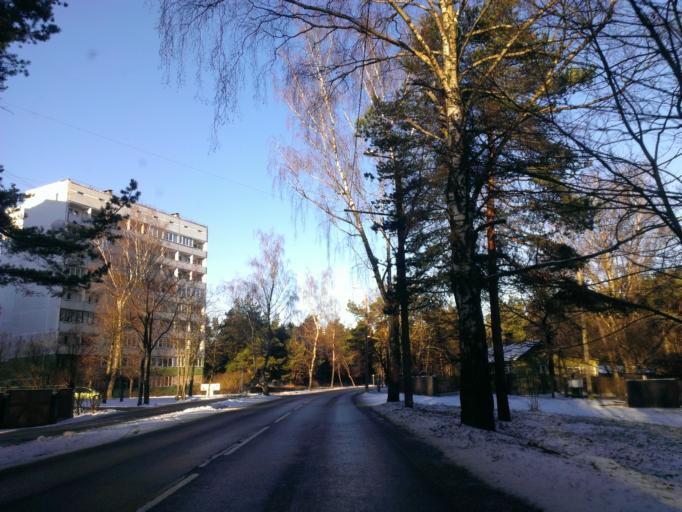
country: LV
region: Riga
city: Bolderaja
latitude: 57.0393
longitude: 24.1038
